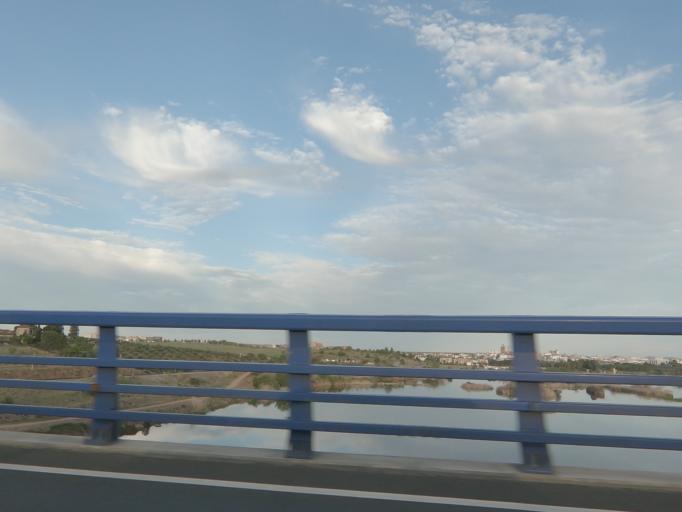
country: ES
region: Extremadura
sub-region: Provincia de Badajoz
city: Merida
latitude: 38.9294
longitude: -6.3680
